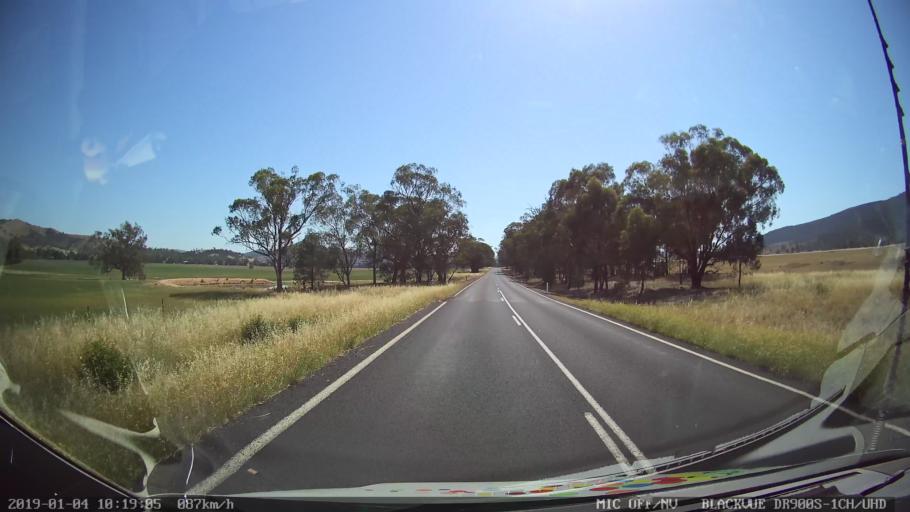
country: AU
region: New South Wales
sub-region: Cabonne
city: Canowindra
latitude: -33.3785
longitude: 148.4755
